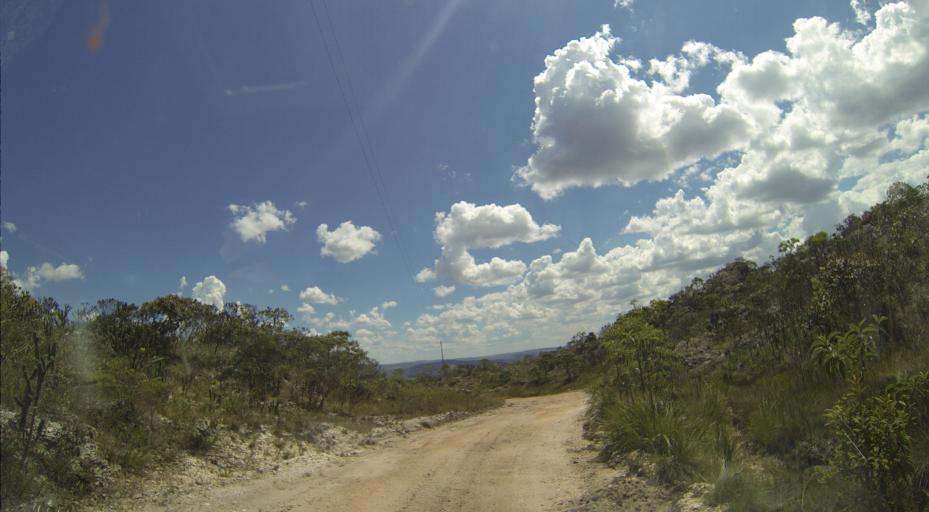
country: BR
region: Minas Gerais
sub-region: Serro
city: Serro
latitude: -18.4631
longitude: -43.4520
